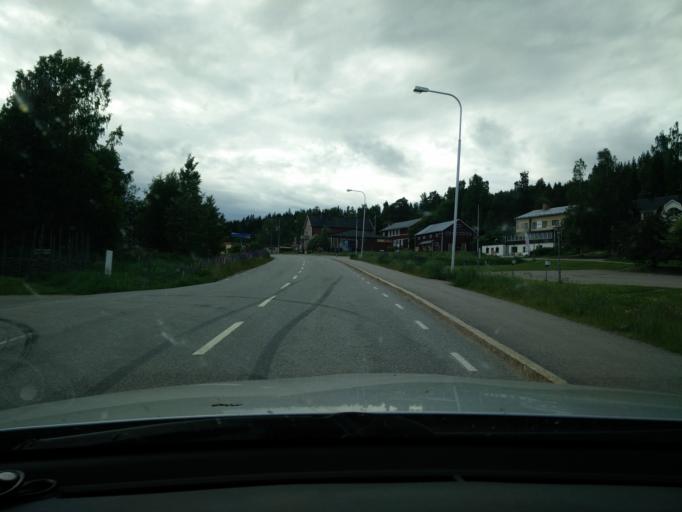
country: SE
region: Gaevleborg
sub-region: Hudiksvalls Kommun
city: Delsbo
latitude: 62.1091
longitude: 16.7126
